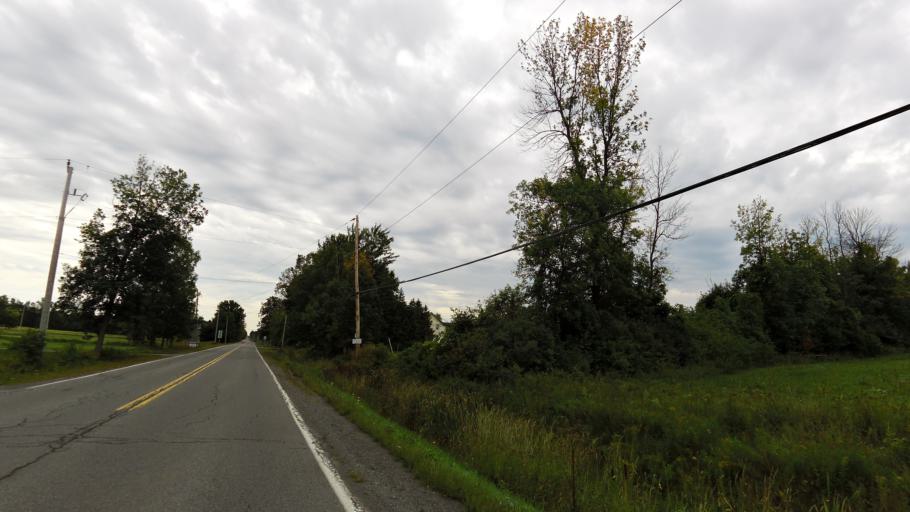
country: CA
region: Ontario
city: Ottawa
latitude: 45.2257
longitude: -75.4675
